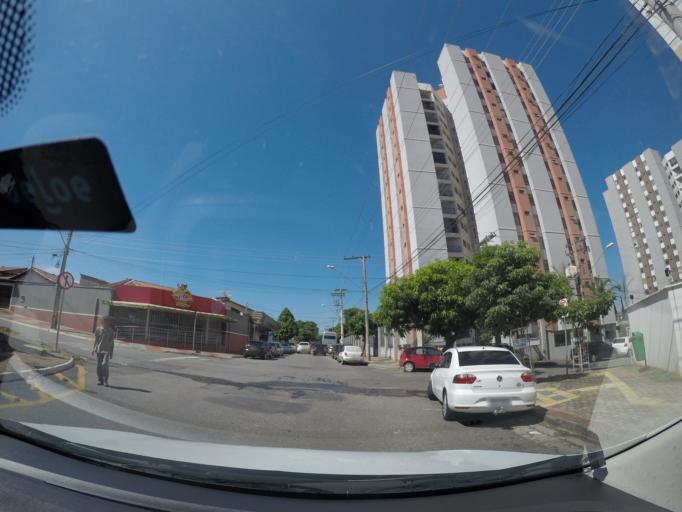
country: BR
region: Goias
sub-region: Goiania
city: Goiania
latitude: -16.6960
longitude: -49.2912
